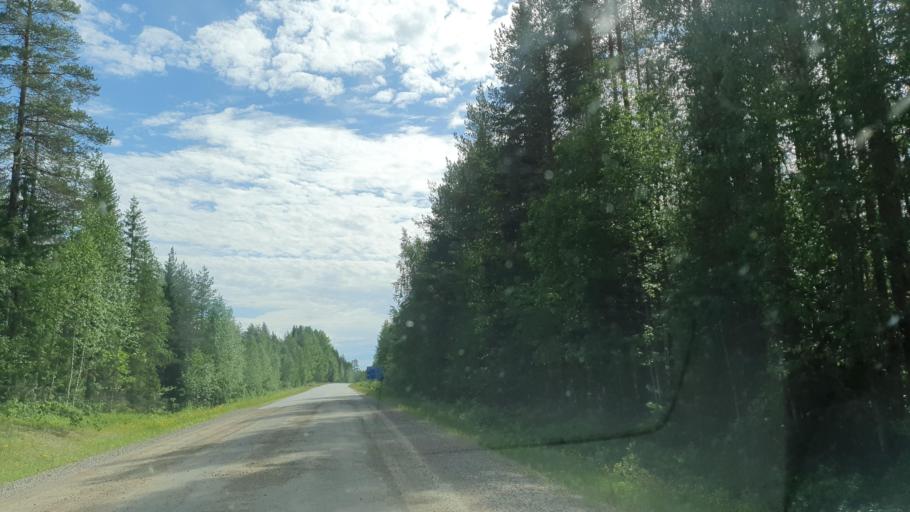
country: FI
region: Kainuu
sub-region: Kehys-Kainuu
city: Kuhmo
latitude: 64.4625
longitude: 29.5359
